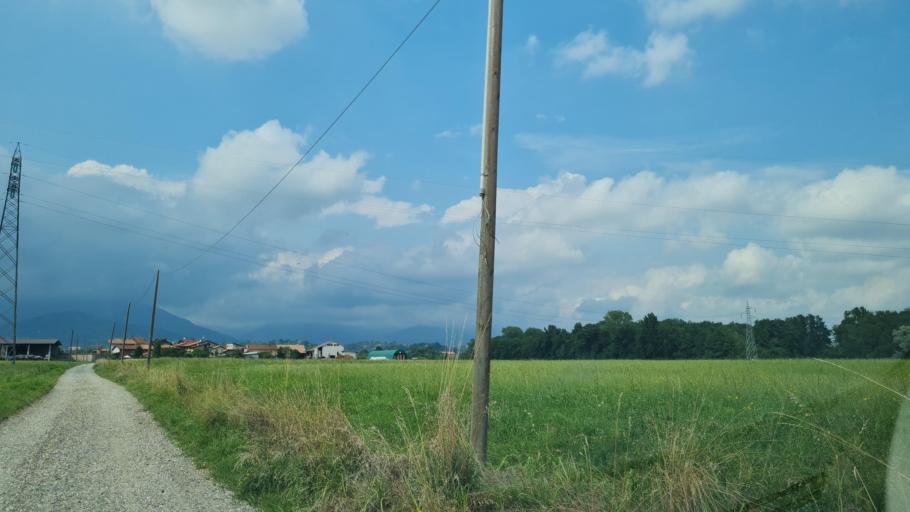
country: IT
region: Piedmont
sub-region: Provincia di Biella
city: Occhieppo Inferiore
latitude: 45.5367
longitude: 8.0314
